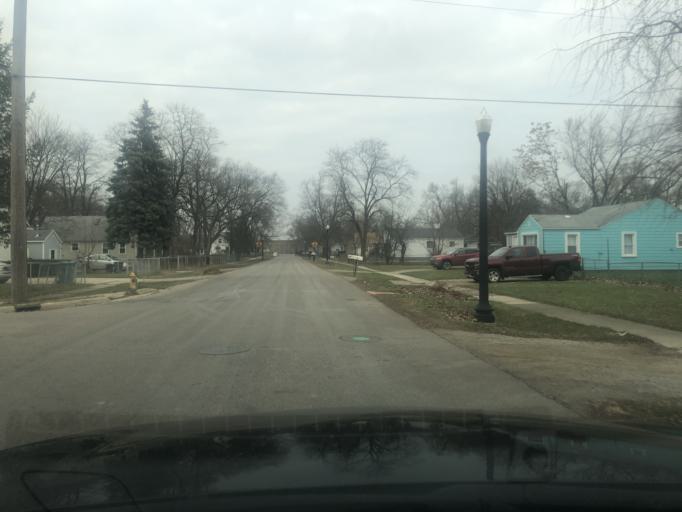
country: US
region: Michigan
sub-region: Wayne County
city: Belleville
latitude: 42.2155
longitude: -83.5492
